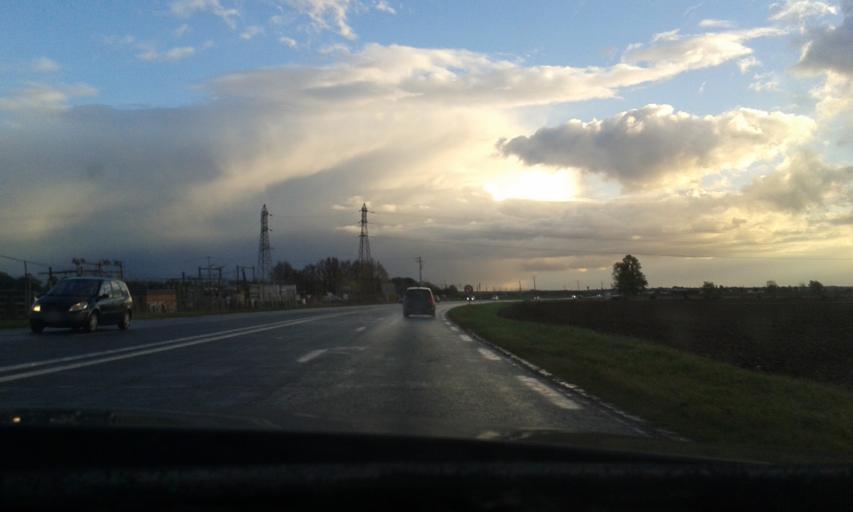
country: FR
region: Centre
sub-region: Departement du Loiret
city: Artenay
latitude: 48.0718
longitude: 1.8773
